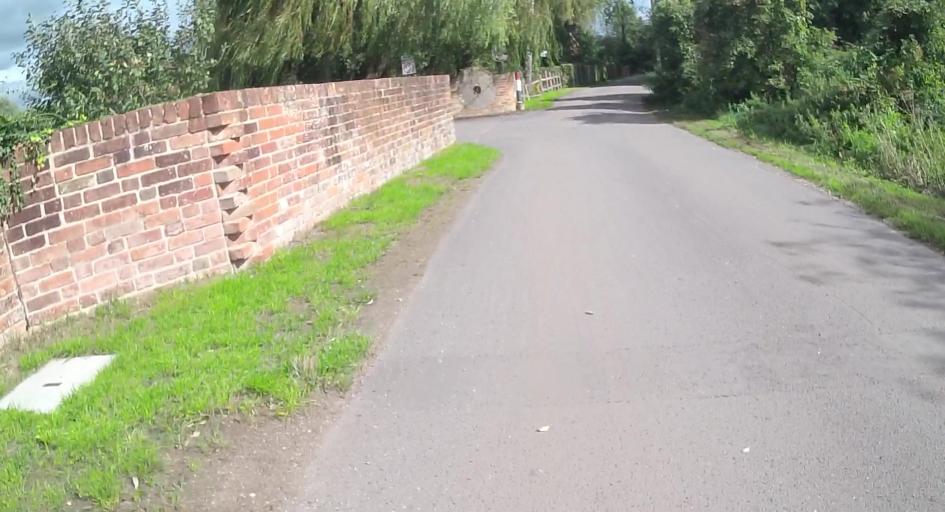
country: GB
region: England
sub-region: West Berkshire
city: Thatcham
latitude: 51.3912
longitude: -1.2402
